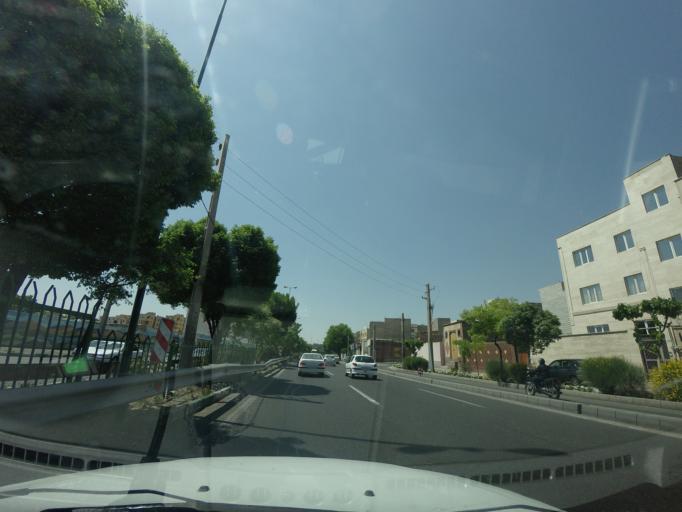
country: IR
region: Tehran
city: Tehran
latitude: 35.6423
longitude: 51.3664
